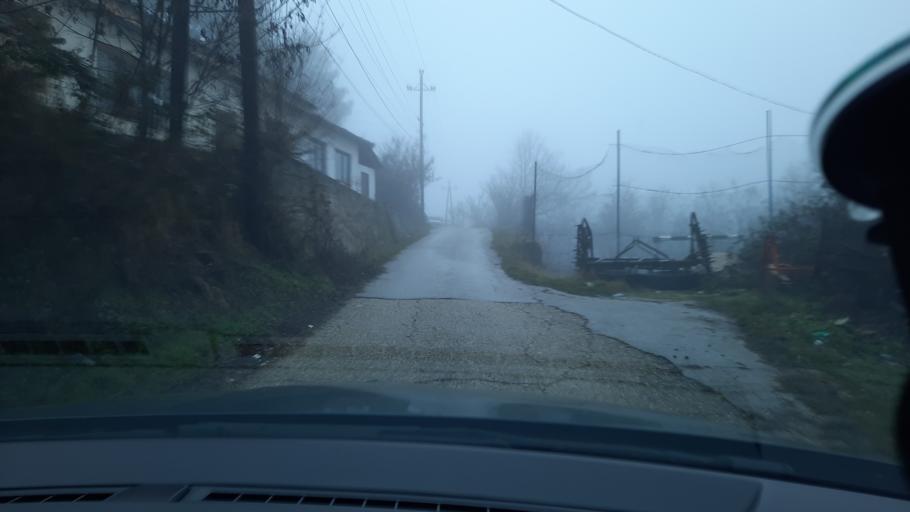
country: MK
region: Vrapciste
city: Vrapciste
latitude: 41.8399
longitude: 20.8805
